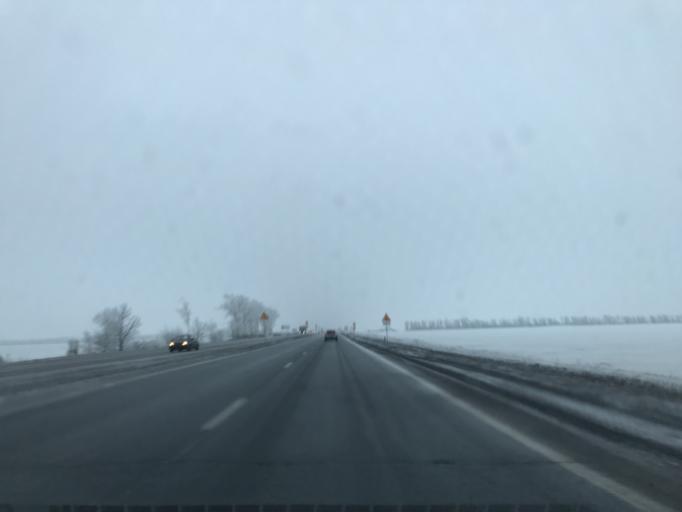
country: RU
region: Rostov
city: Grushevskaya
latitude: 47.4952
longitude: 39.9707
